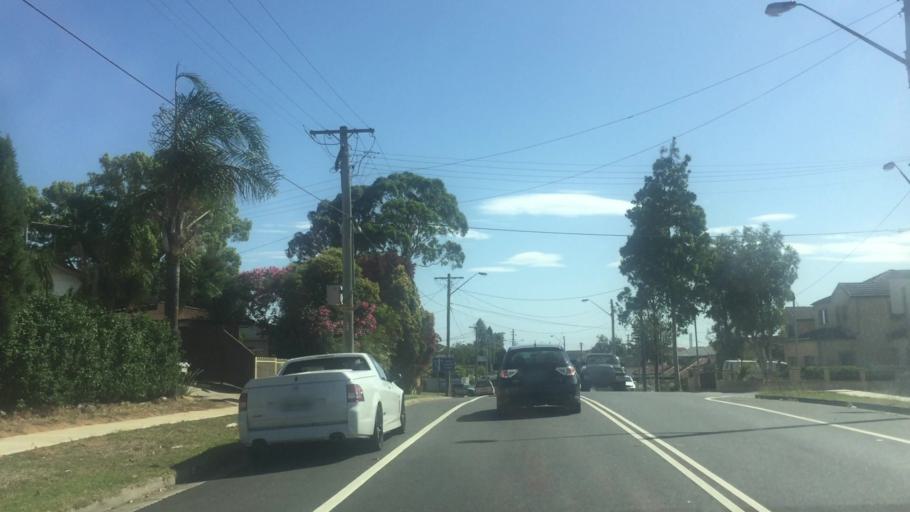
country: AU
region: New South Wales
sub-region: Holroyd
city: Merrylands
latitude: -33.8255
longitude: 150.9853
